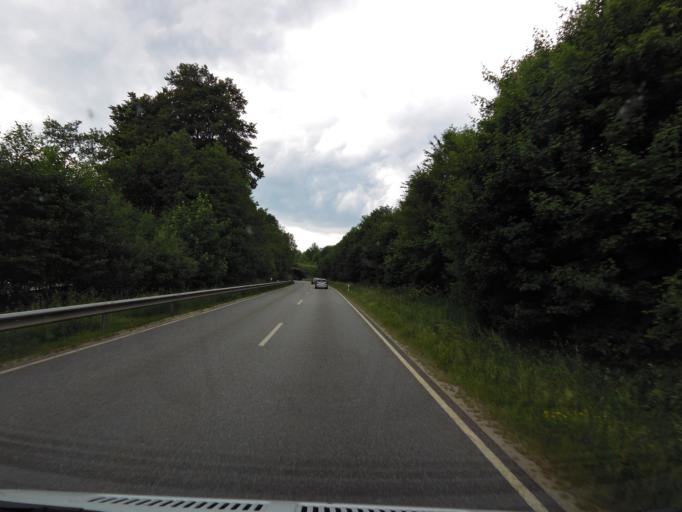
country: DE
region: Bavaria
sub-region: Lower Bavaria
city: Neukirchen vorm Wald
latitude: 48.6807
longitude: 13.3528
